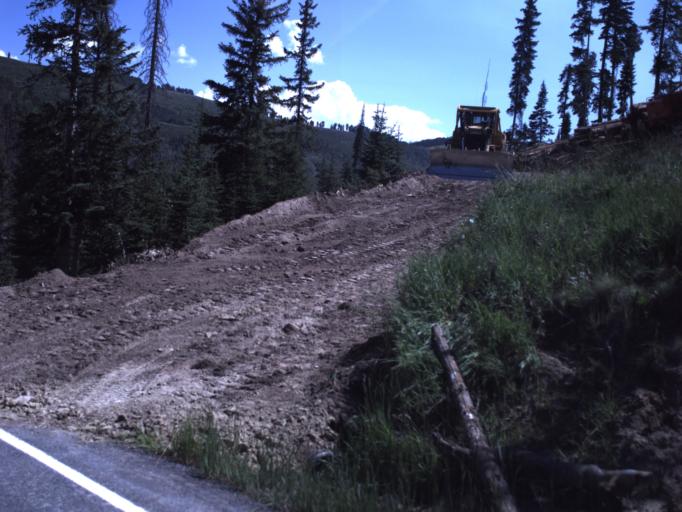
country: US
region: Utah
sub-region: Sanpete County
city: Fairview
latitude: 39.6786
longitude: -111.2122
